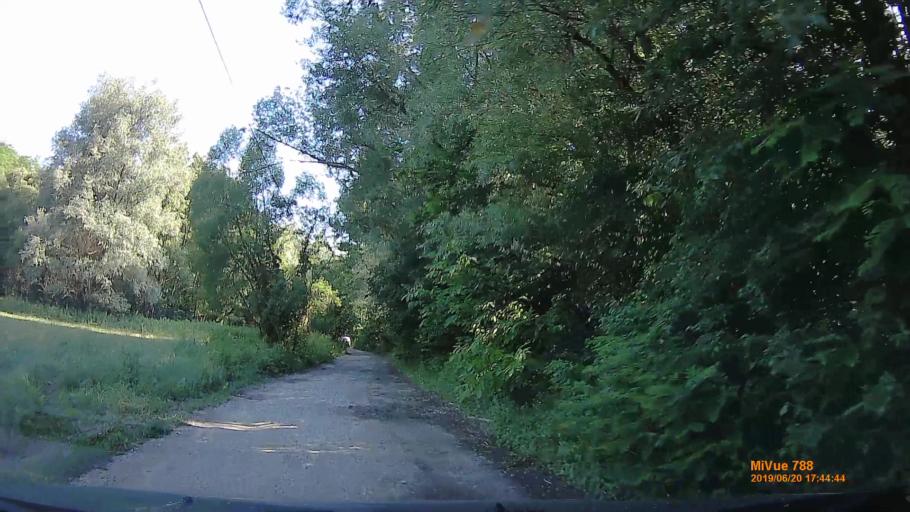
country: HU
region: Baranya
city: Buekkoesd
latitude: 46.1354
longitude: 18.0027
